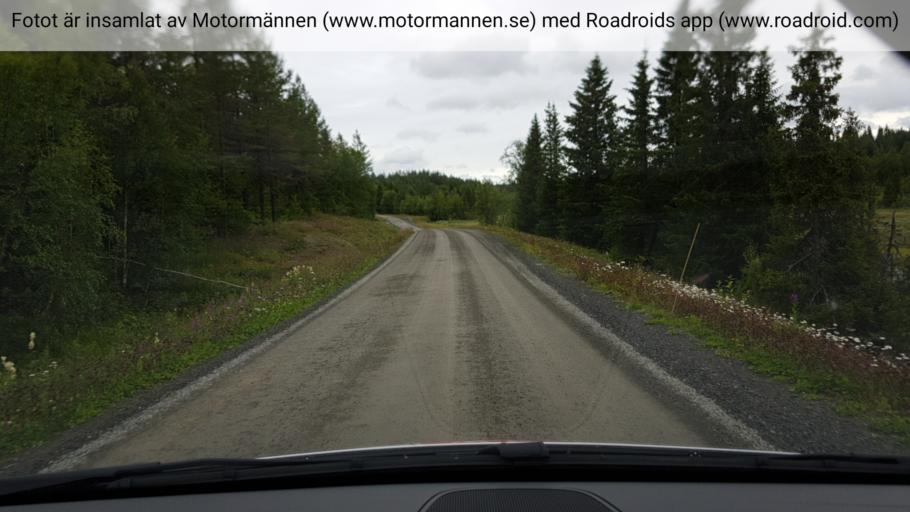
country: SE
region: Jaemtland
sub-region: Krokoms Kommun
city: Krokom
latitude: 63.7366
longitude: 14.4894
